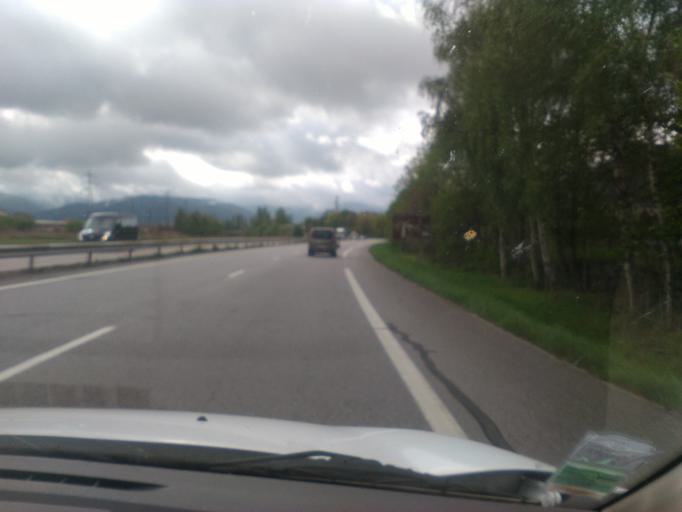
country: FR
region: Lorraine
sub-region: Departement des Vosges
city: Remiremont
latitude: 48.0231
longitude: 6.5930
